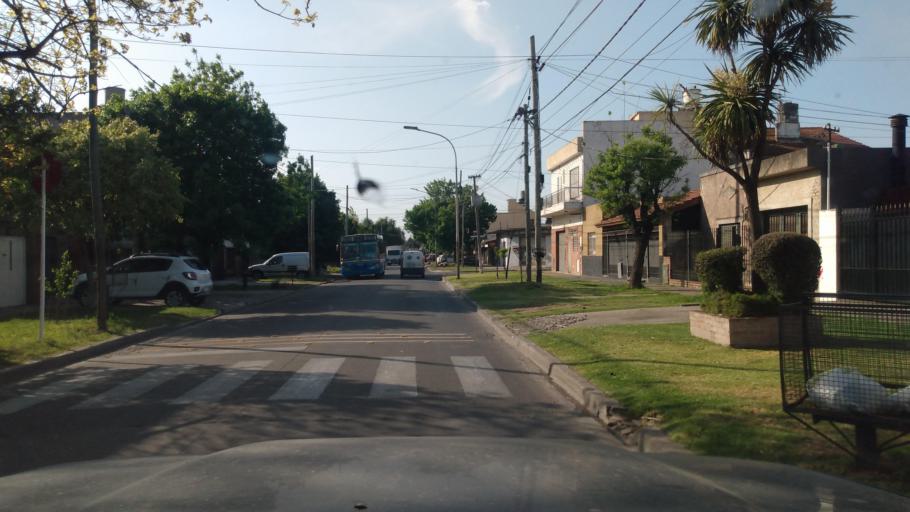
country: AR
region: Buenos Aires
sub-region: Partido de Moron
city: Moron
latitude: -34.6584
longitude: -58.5954
